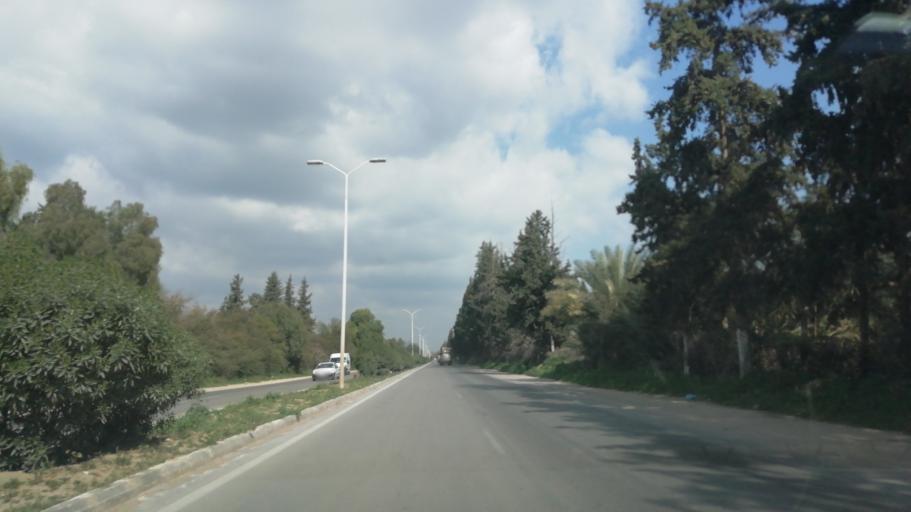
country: DZ
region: Mascara
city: Mascara
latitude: 35.5990
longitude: 0.0810
